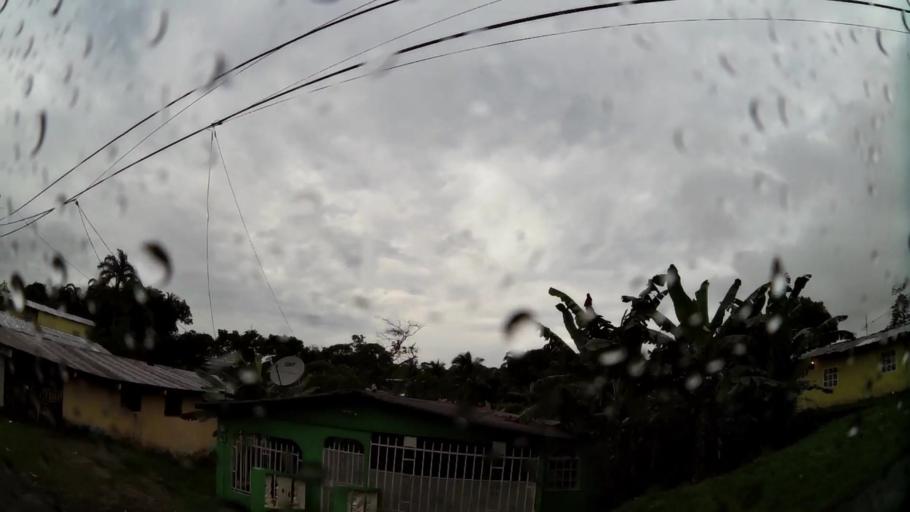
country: PA
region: Colon
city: Arco Iris
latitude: 9.3366
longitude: -79.8653
